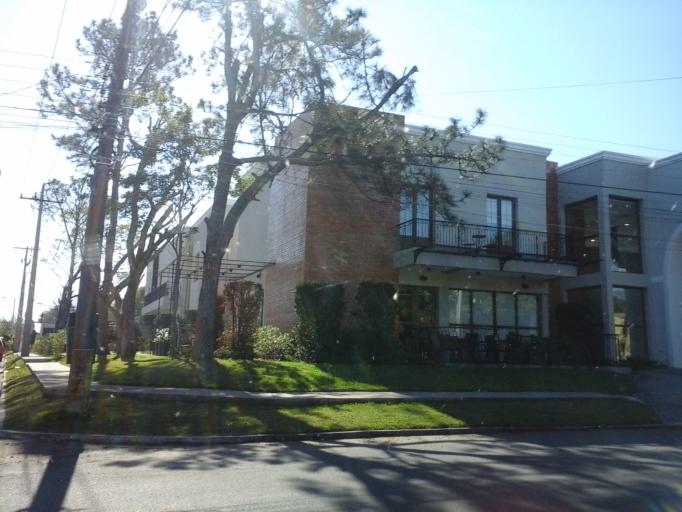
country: PY
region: Neembucu
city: Pilar
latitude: -26.8623
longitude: -58.3051
